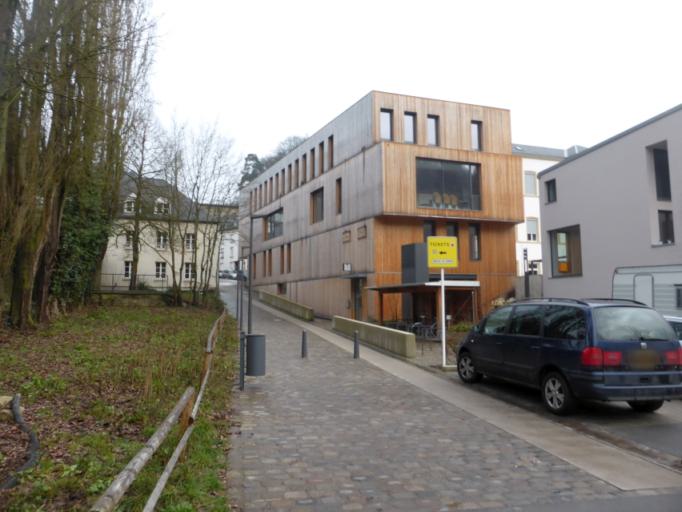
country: LU
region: Luxembourg
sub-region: Canton de Luxembourg
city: Luxembourg
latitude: 49.6147
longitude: 6.1328
